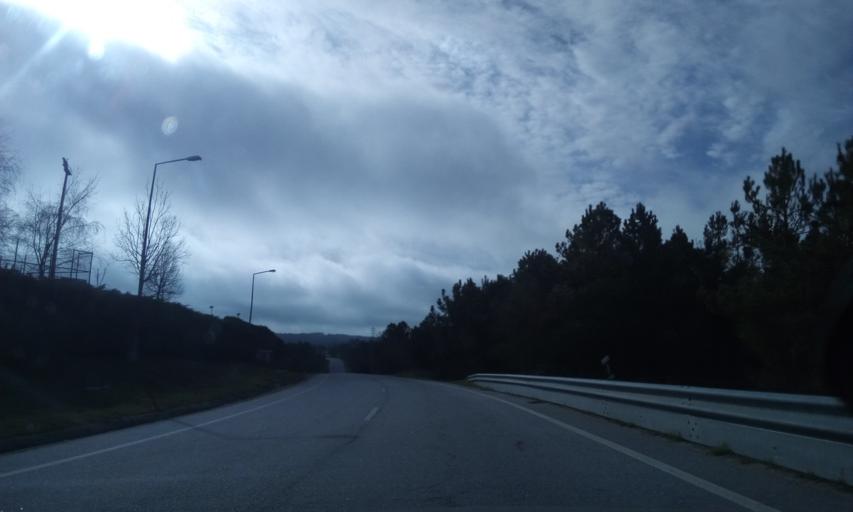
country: PT
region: Guarda
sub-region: Aguiar da Beira
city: Aguiar da Beira
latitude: 40.8134
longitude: -7.5362
